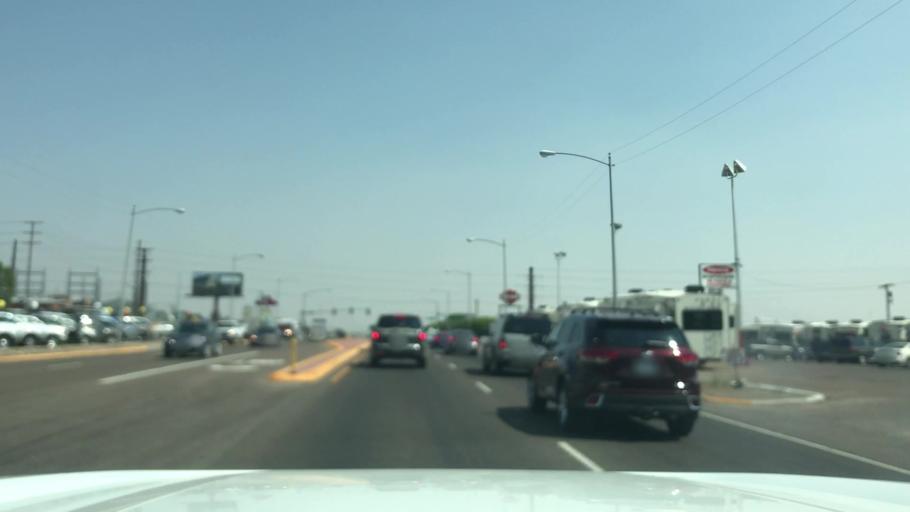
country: US
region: Montana
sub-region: Cascade County
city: Malmstrom Air Force Base
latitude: 47.4939
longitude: -111.2358
